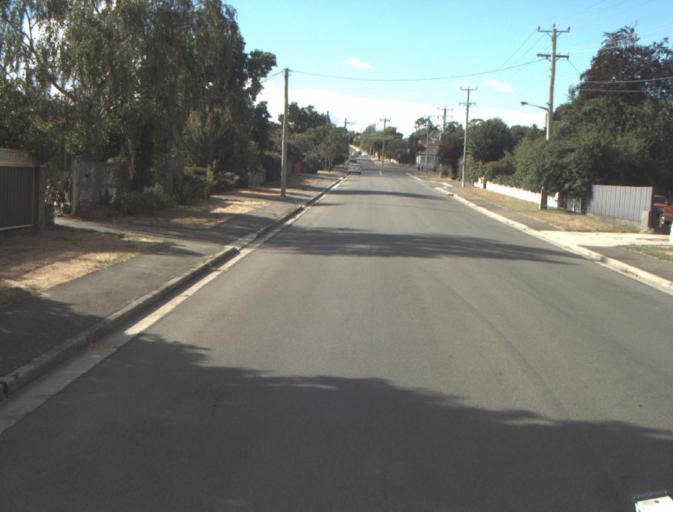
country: AU
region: Tasmania
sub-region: Launceston
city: Newstead
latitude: -41.4569
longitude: 147.1732
